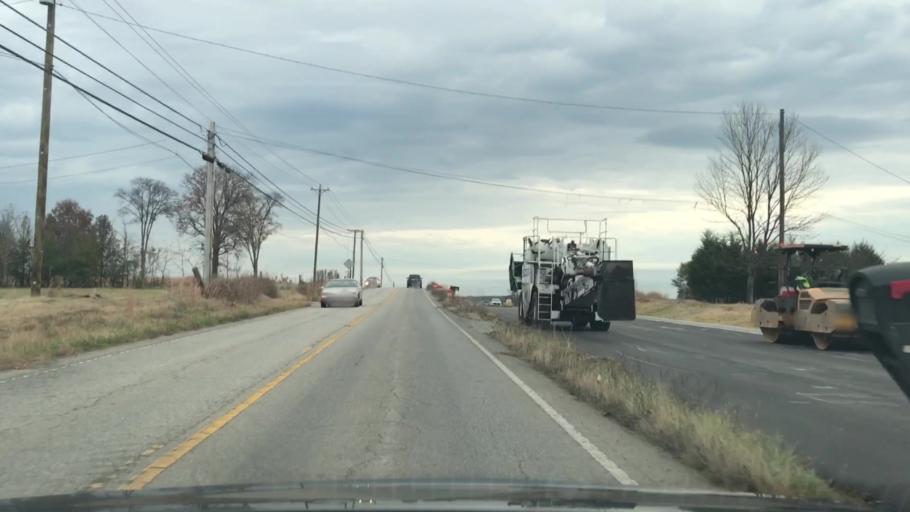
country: US
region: Tennessee
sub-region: Wilson County
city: Lebanon
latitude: 36.2439
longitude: -86.2561
